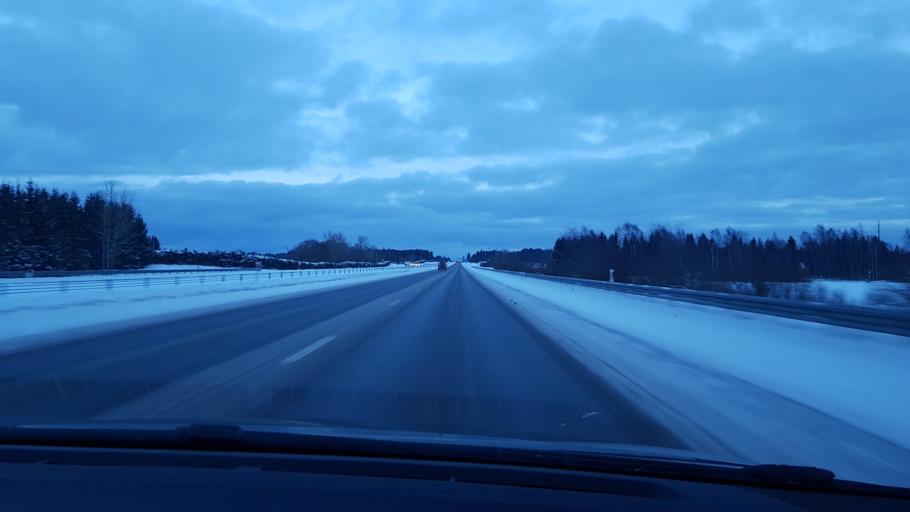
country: EE
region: Harju
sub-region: Kuusalu vald
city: Kuusalu
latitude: 59.4460
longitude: 25.3905
